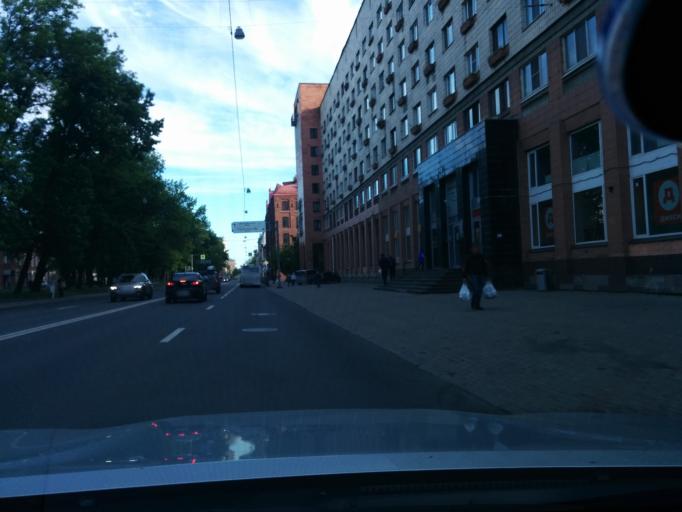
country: RU
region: Leningrad
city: Sampsonievskiy
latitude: 59.9759
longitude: 30.3386
